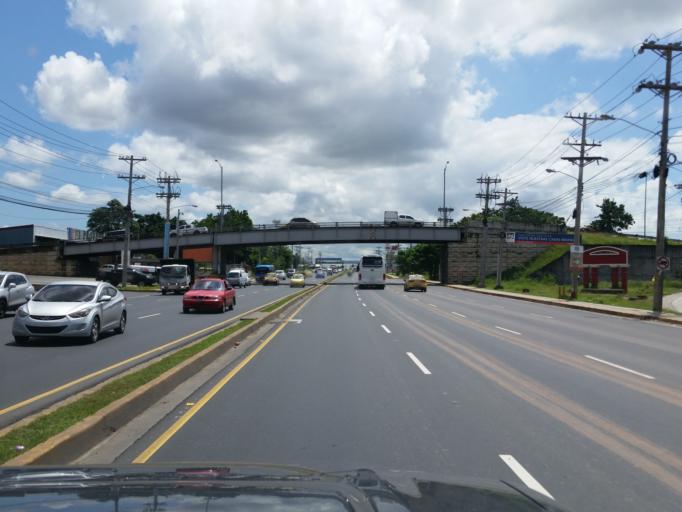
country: PA
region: Panama
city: San Miguelito
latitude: 9.0603
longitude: -79.4275
